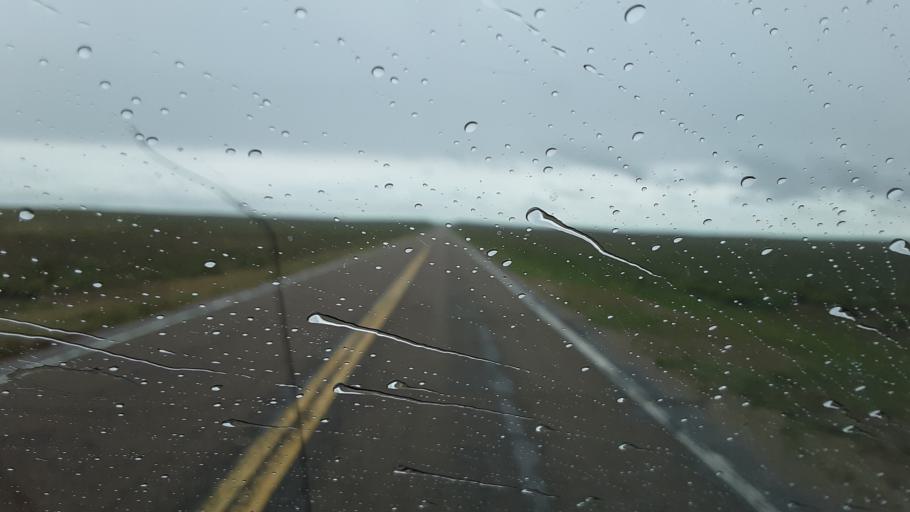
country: US
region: Colorado
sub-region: Lincoln County
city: Hugo
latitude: 38.8494
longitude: -103.2439
